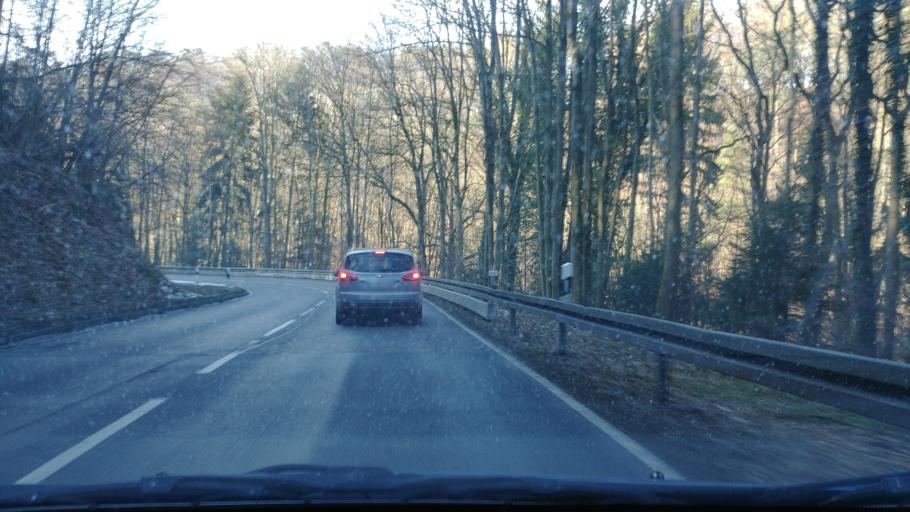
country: DE
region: Lower Saxony
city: Bad Karlshafen
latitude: 51.6314
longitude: 9.4492
